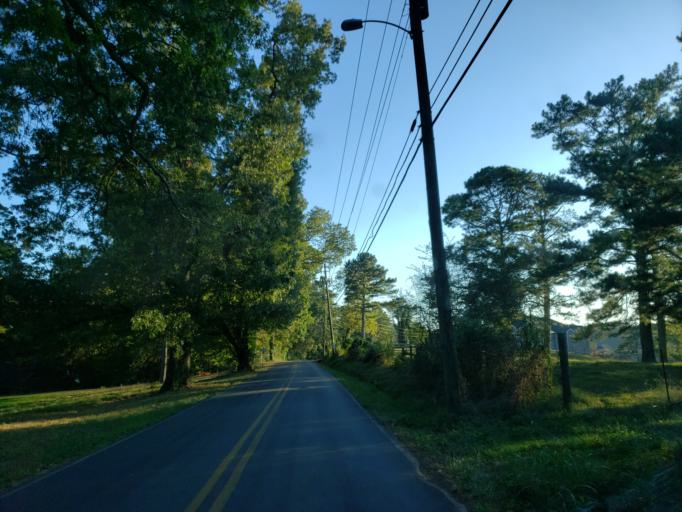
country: US
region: Georgia
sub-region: Pickens County
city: Jasper
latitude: 34.4621
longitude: -84.4325
